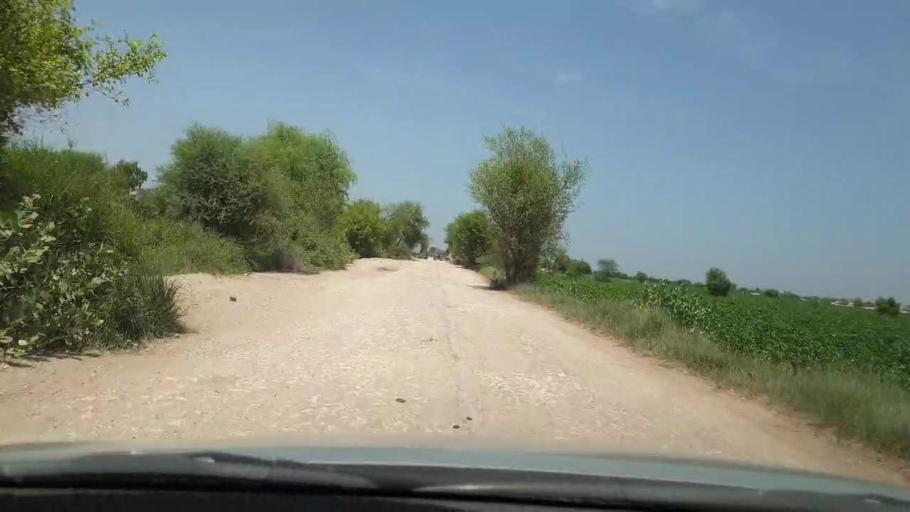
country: PK
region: Sindh
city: Pano Aqil
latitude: 27.7002
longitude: 69.2177
